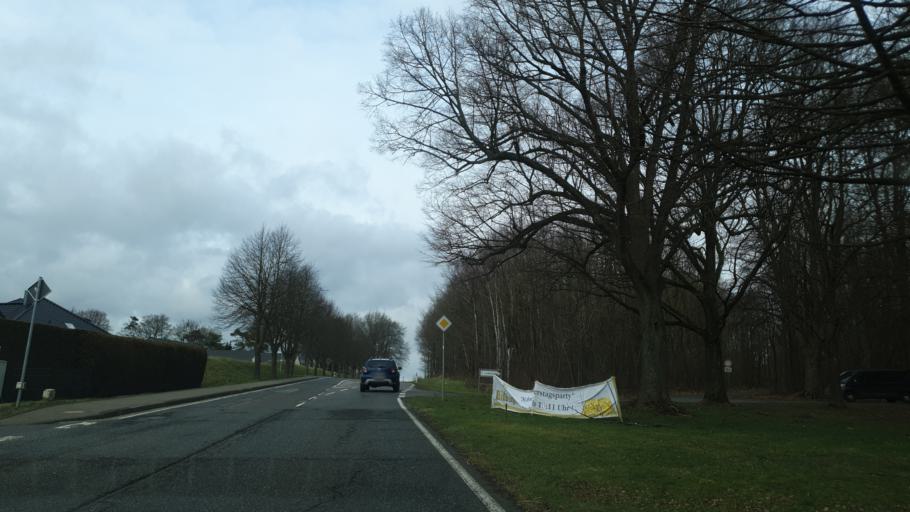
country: DE
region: Rheinland-Pfalz
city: Urbach-Uberdorf
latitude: 50.5664
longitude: 7.5894
